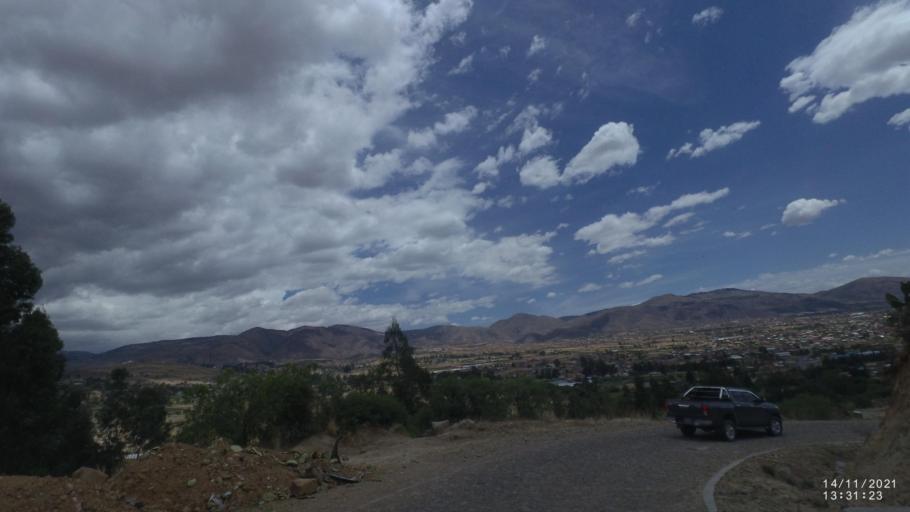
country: BO
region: Cochabamba
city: Colomi
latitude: -17.3952
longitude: -65.9813
